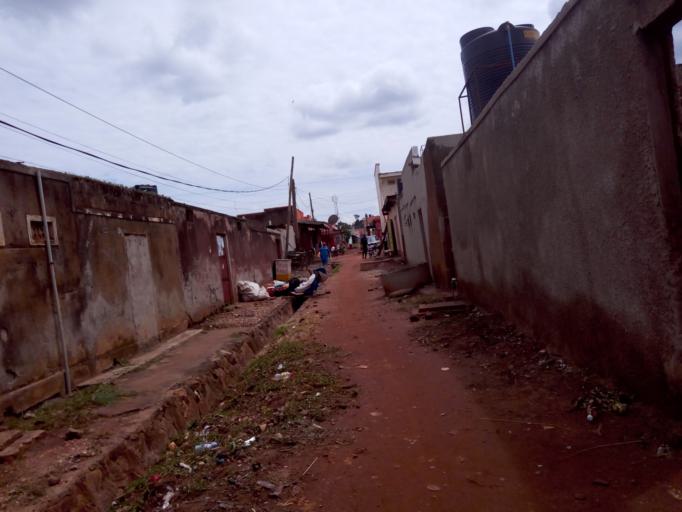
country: UG
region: Western Region
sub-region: Masindi District
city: Masindi
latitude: 1.6828
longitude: 31.7221
